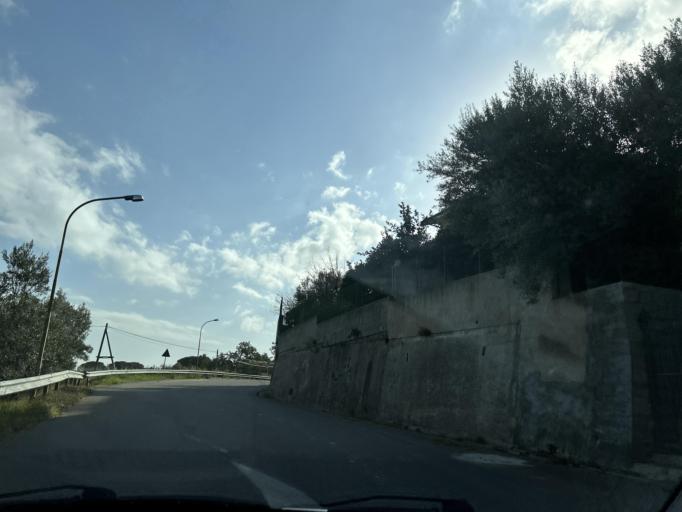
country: IT
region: Calabria
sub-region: Provincia di Catanzaro
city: Montepaone
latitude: 38.7231
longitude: 16.5086
